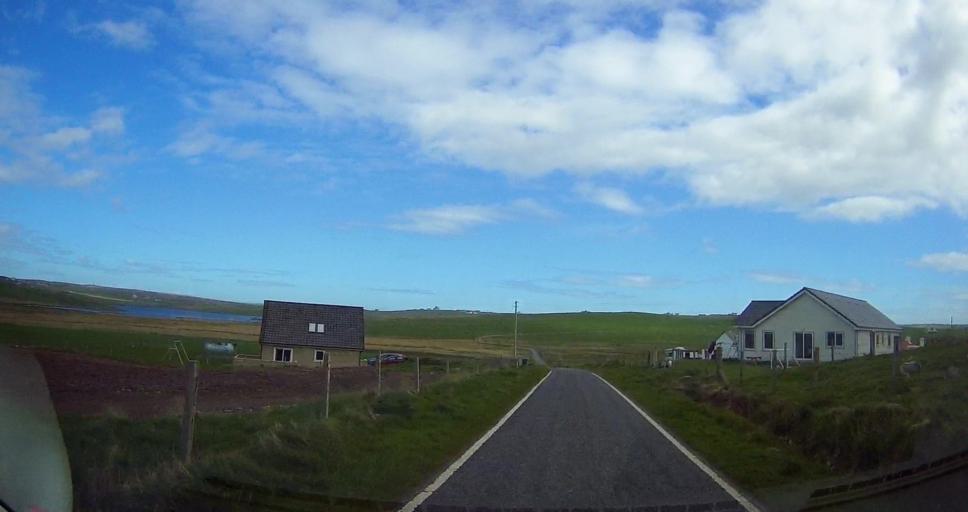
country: GB
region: Scotland
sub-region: Shetland Islands
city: Sandwick
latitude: 59.9234
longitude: -1.3316
